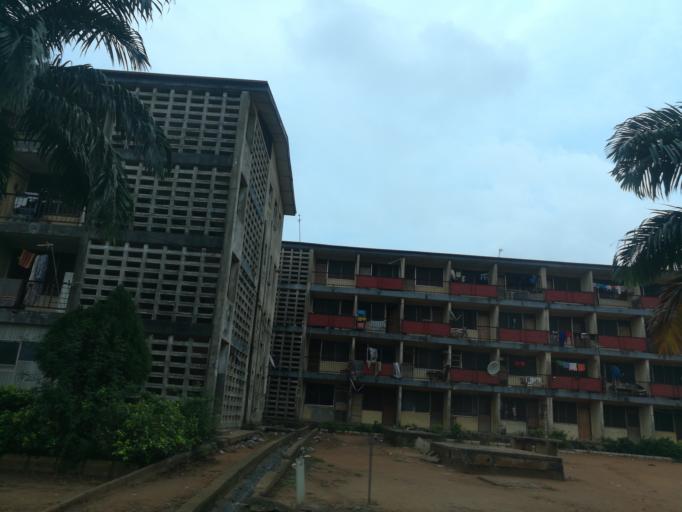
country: NG
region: Lagos
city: Oshodi
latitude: 6.5688
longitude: 3.3548
